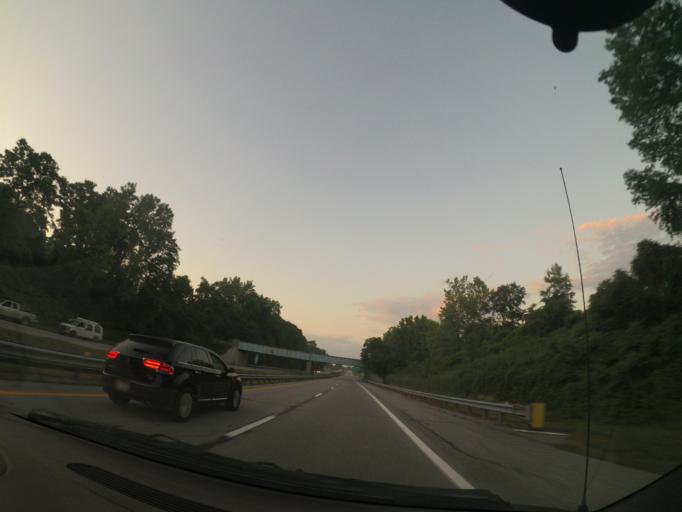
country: US
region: Ohio
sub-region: Lake County
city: Painesville
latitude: 41.7436
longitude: -81.2207
